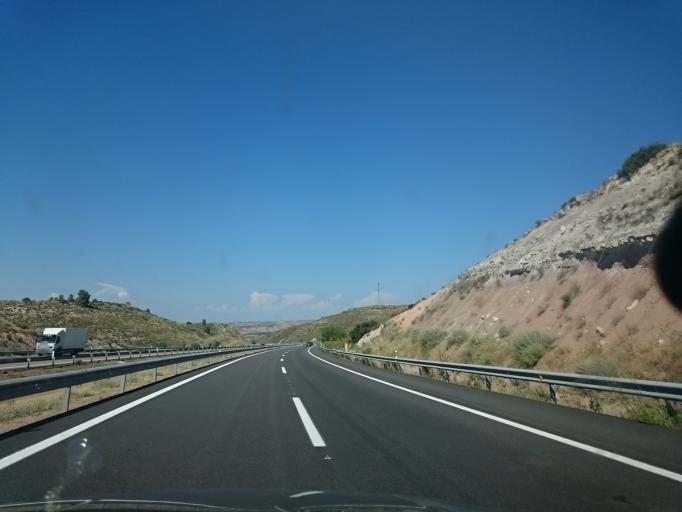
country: ES
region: Aragon
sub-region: Provincia de Huesca
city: Fraga
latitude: 41.4709
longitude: 0.3074
